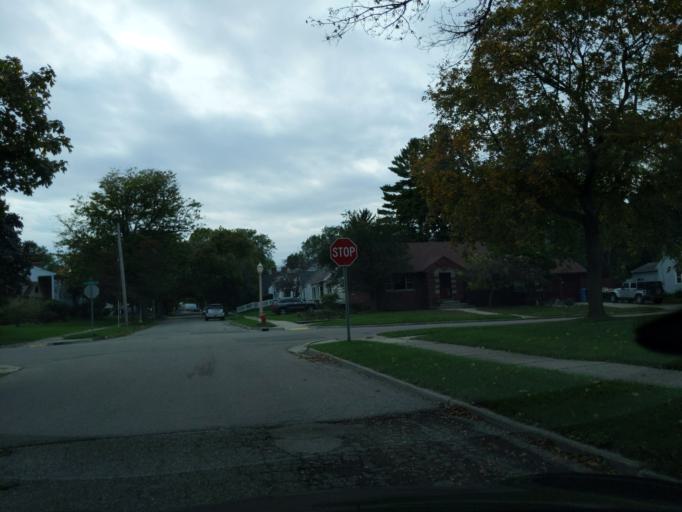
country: US
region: Michigan
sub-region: Ingham County
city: Lansing
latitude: 42.7136
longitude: -84.5350
